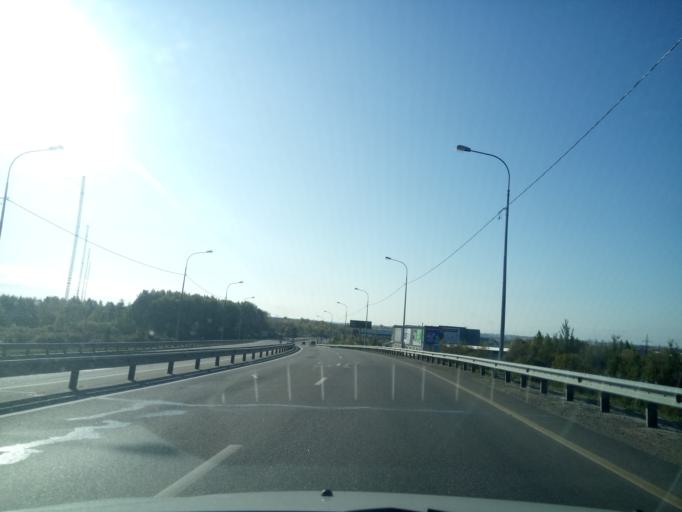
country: RU
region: Nizjnij Novgorod
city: Burevestnik
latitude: 56.1757
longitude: 43.9137
